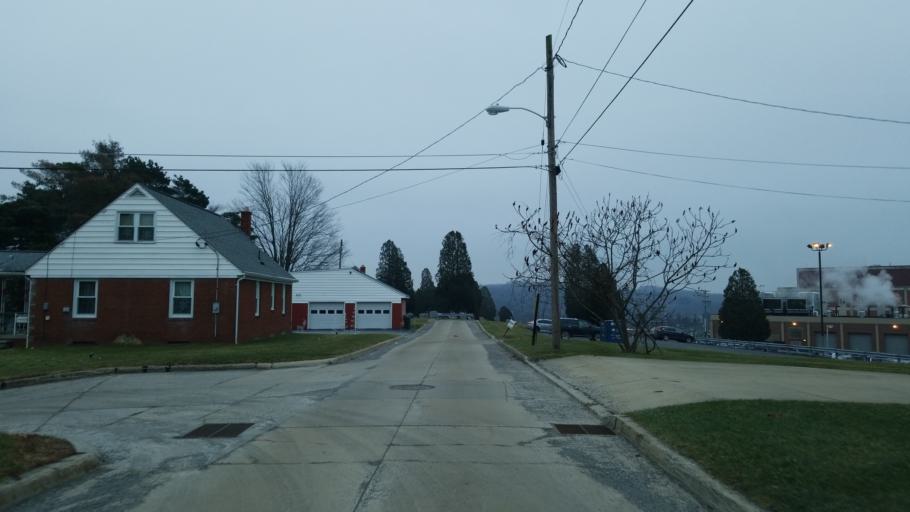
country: US
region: Pennsylvania
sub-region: Clearfield County
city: Sandy
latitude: 41.1168
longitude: -78.7757
